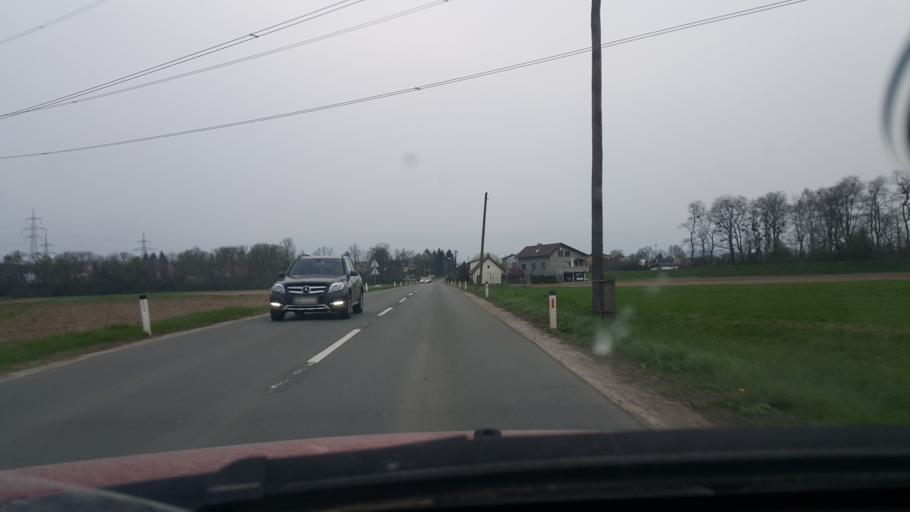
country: SI
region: Duplek
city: Zgornji Duplek
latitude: 46.5178
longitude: 15.7081
